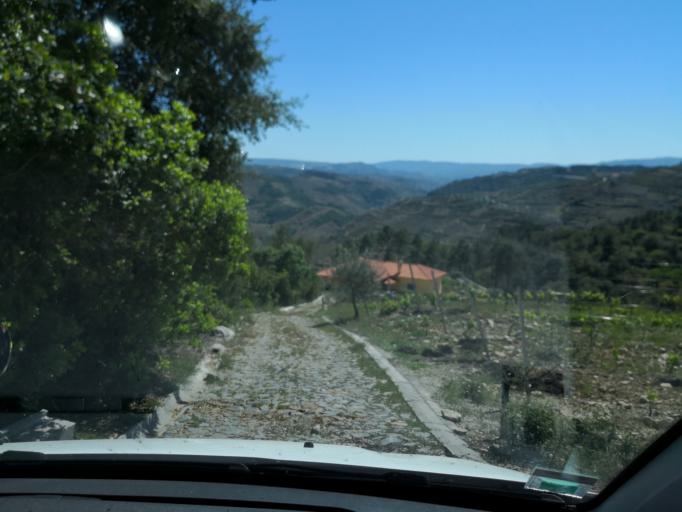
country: PT
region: Vila Real
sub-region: Vila Real
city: Vila Real
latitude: 41.2416
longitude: -7.7191
